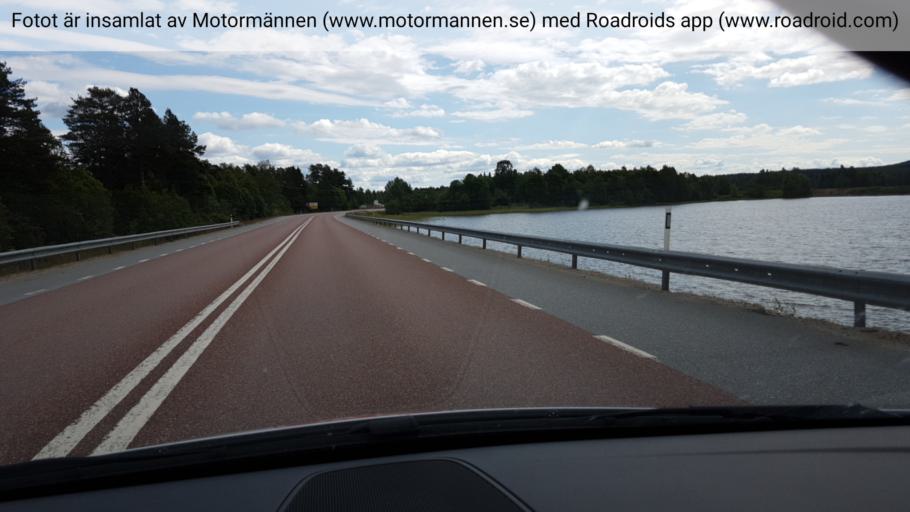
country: SE
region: Jaemtland
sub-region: Braecke Kommun
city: Braecke
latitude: 62.9182
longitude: 15.2448
